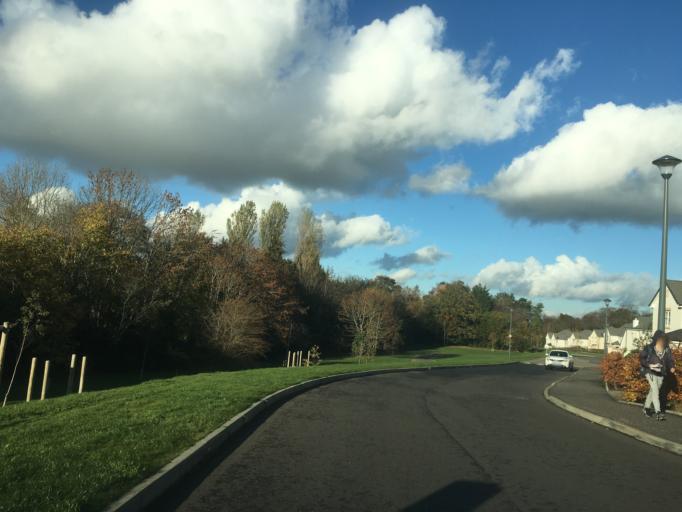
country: GB
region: Scotland
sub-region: Edinburgh
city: Colinton
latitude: 55.8998
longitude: -3.2503
